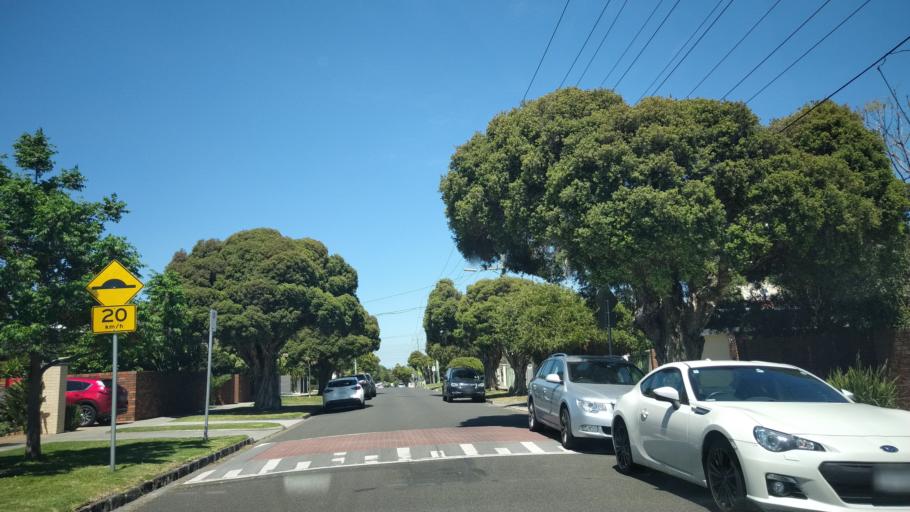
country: AU
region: Victoria
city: Ormond
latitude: -37.8953
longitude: 145.0319
